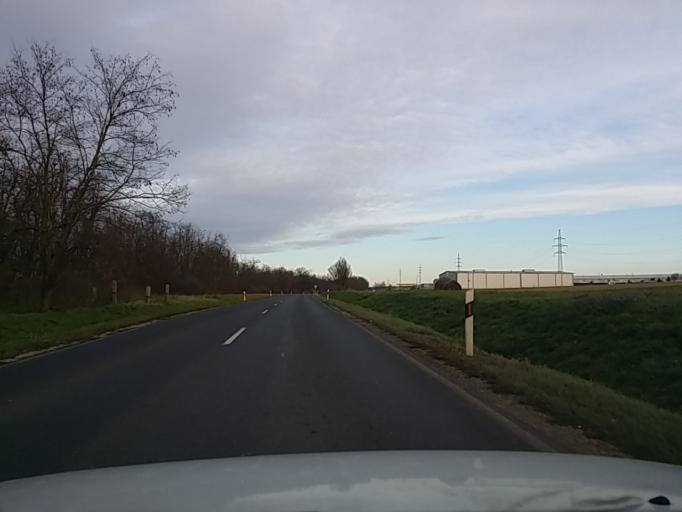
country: HU
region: Veszprem
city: Nemesvamos
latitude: 47.0619
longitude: 17.8650
